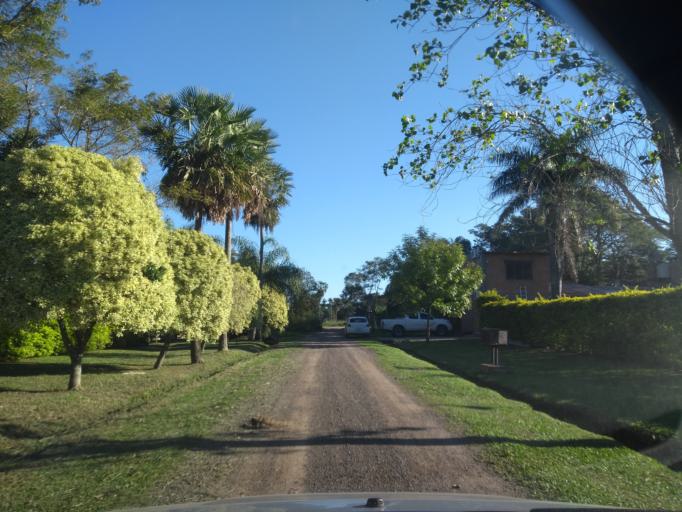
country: AR
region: Chaco
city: Barranqueras
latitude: -27.4392
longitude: -58.9079
